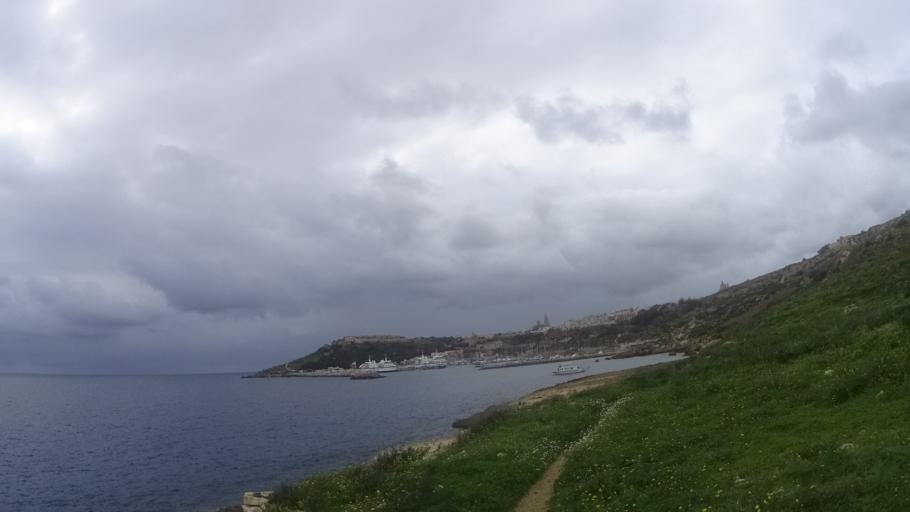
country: MT
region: Il-Qala
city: Qala
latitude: 36.0266
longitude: 14.3075
